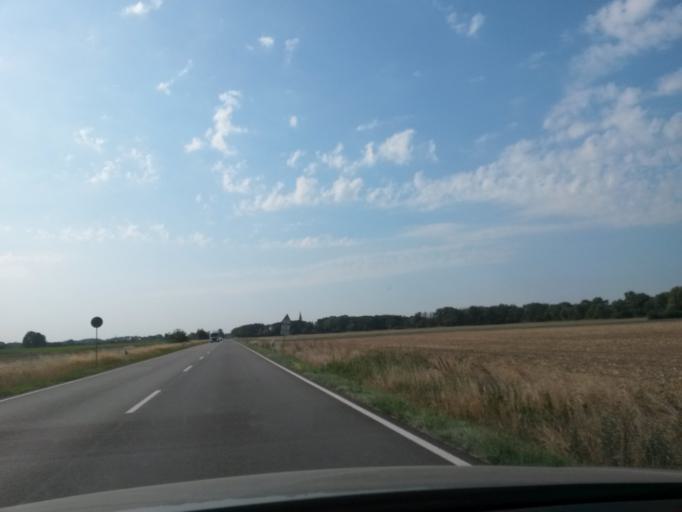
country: DE
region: Saxony-Anhalt
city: Jerichow
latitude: 52.5154
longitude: 12.0159
